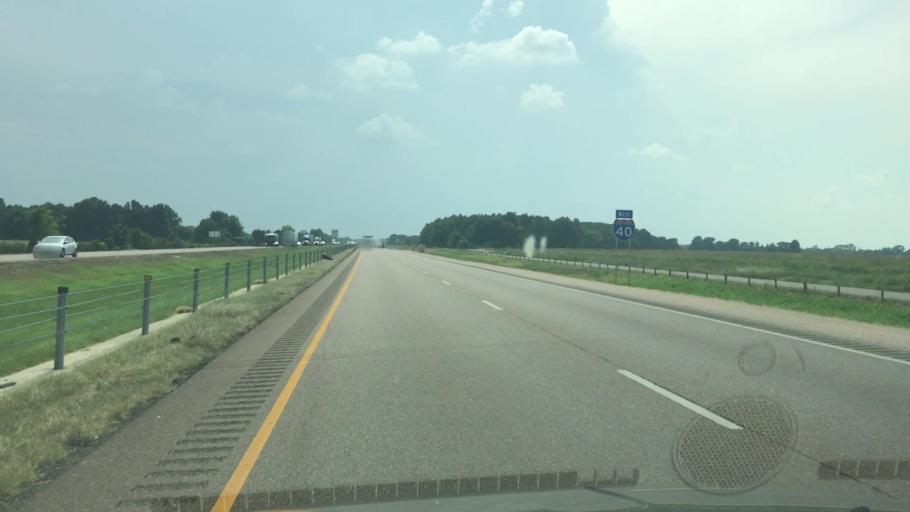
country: US
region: Arkansas
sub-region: Crittenden County
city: Earle
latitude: 35.1494
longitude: -90.4062
